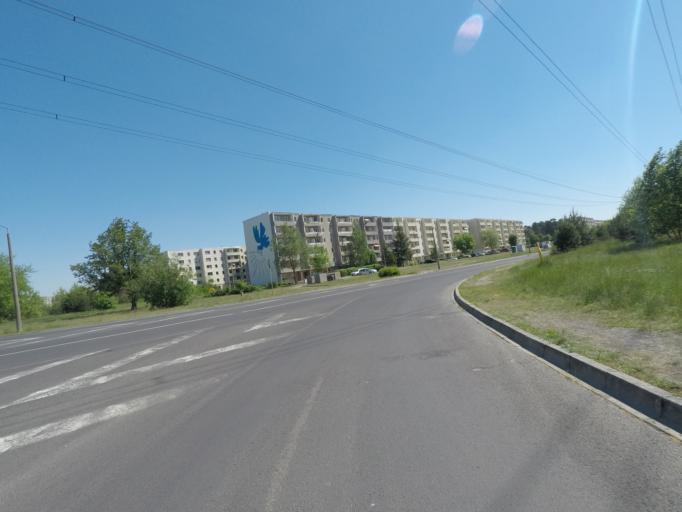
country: DE
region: Brandenburg
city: Eberswalde
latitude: 52.8343
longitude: 13.7515
